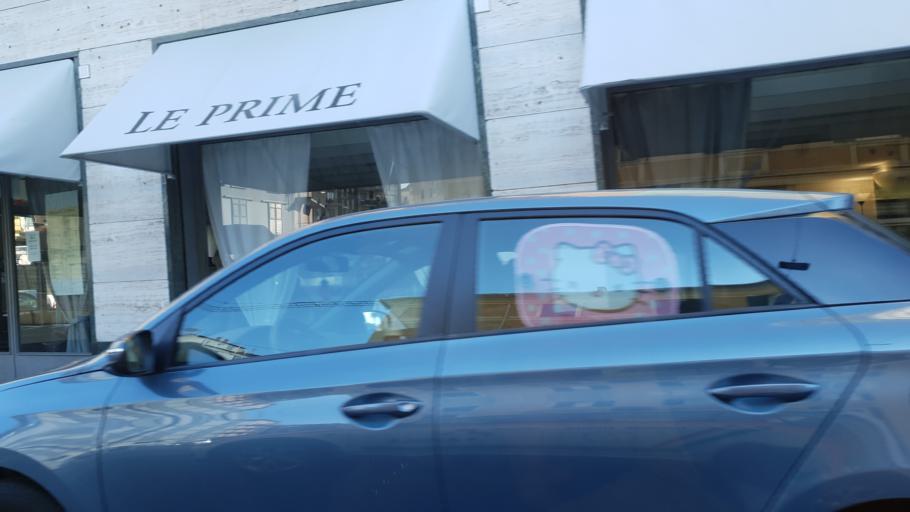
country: IT
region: Liguria
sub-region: Provincia di Savona
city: Vado Ligure
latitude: 44.2727
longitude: 8.4385
